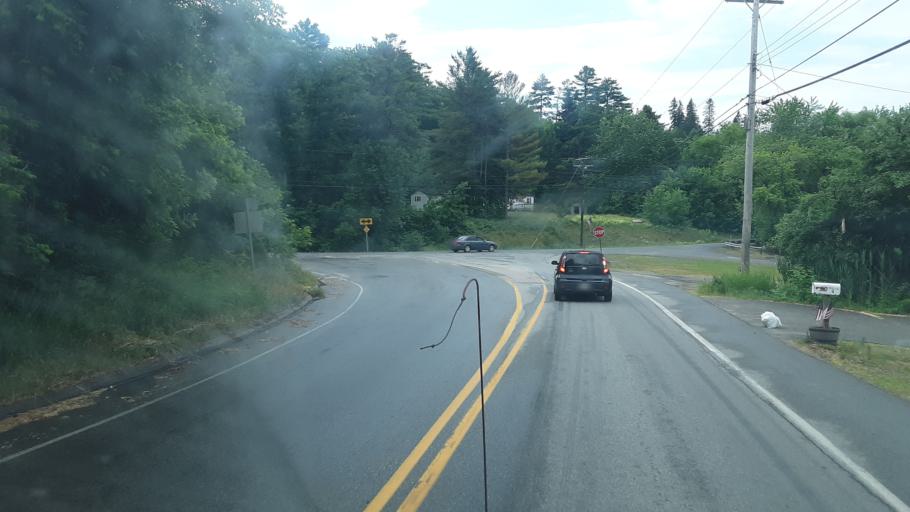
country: US
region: Maine
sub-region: Penobscot County
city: Eddington
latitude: 44.8248
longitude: -68.6934
